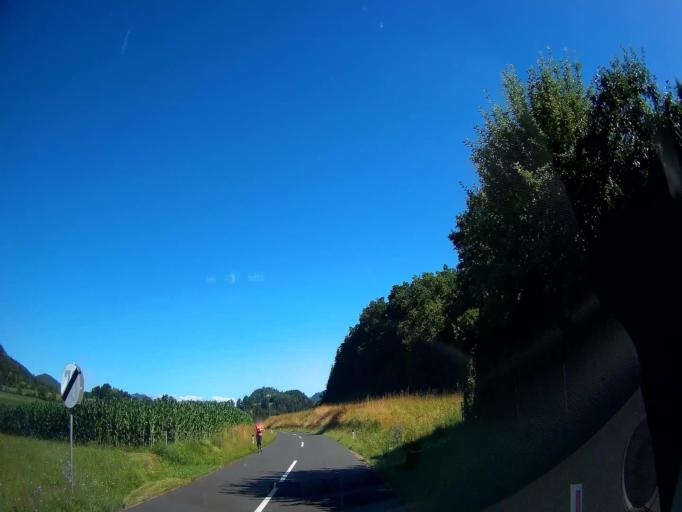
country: AT
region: Carinthia
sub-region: Politischer Bezirk Volkermarkt
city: Voelkermarkt
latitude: 46.6777
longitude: 14.5787
